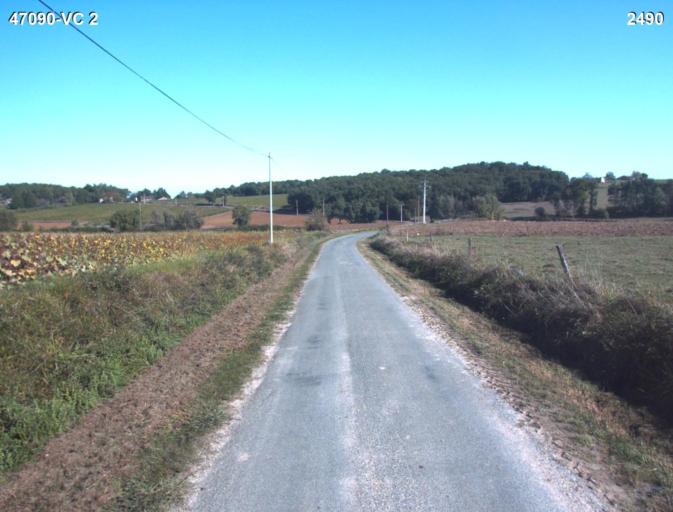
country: FR
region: Aquitaine
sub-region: Departement du Lot-et-Garonne
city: Nerac
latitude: 44.1728
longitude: 0.3759
